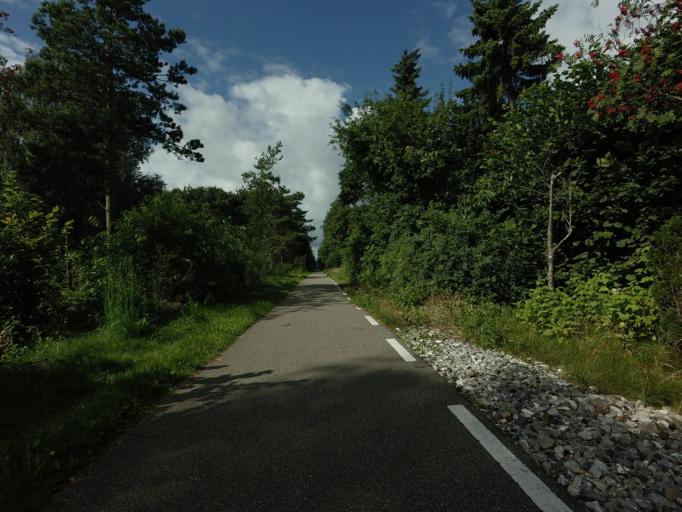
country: DK
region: Central Jutland
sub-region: Silkeborg Kommune
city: Svejbaek
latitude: 56.1751
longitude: 9.6265
